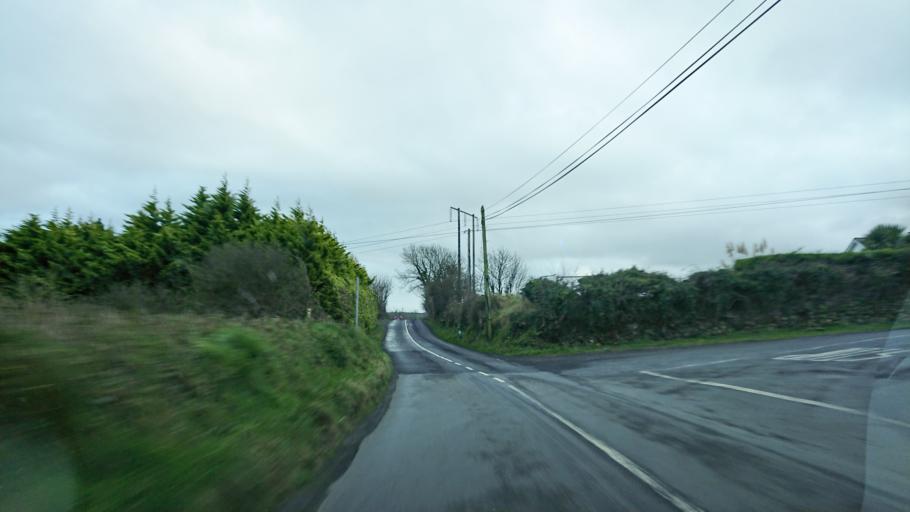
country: IE
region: Munster
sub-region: Waterford
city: Portlaw
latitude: 52.1707
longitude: -7.3955
